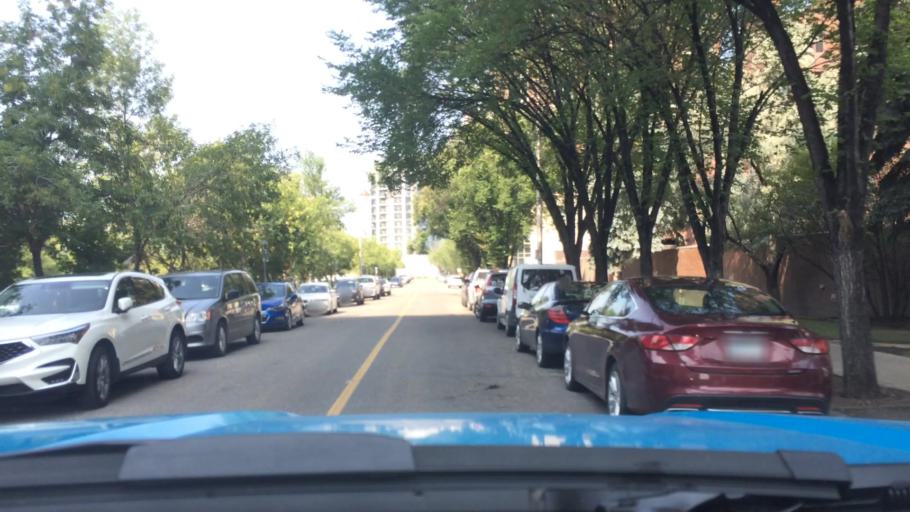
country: CA
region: Alberta
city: Calgary
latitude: 51.0526
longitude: -114.0718
